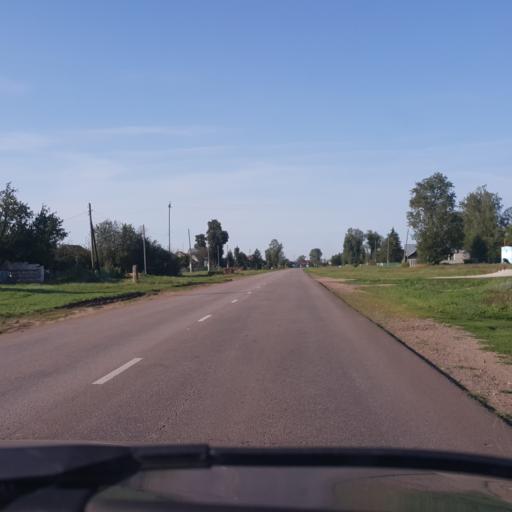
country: RU
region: Tambov
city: Novaya Lyada
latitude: 52.7801
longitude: 41.7601
